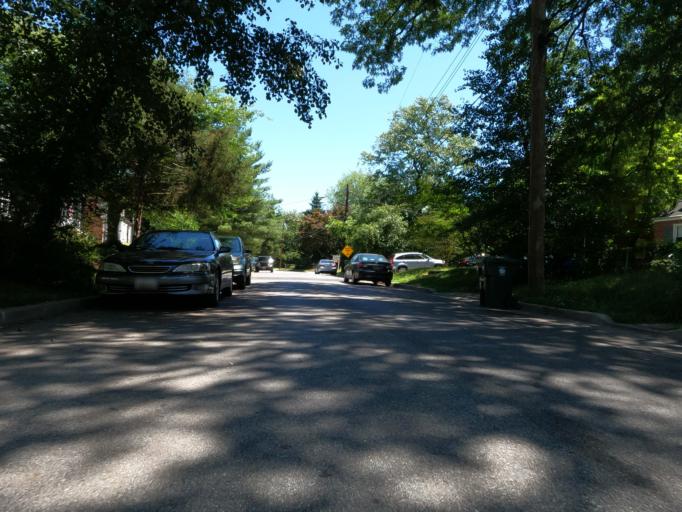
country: US
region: Maryland
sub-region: Prince George's County
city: Berwyn Heights
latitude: 38.9923
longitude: -76.9252
